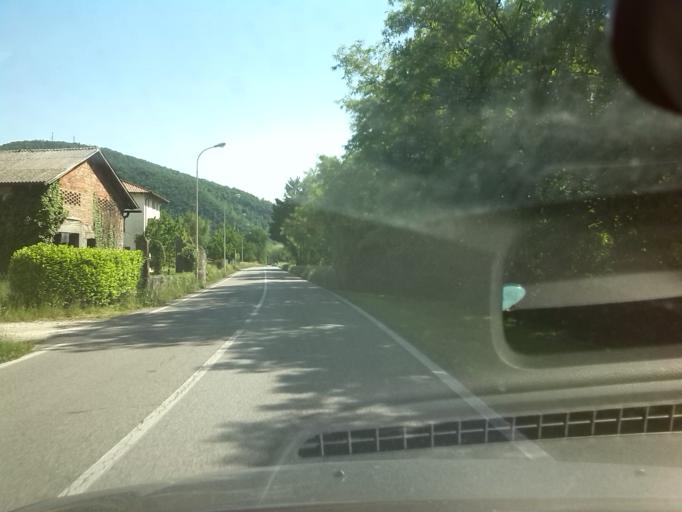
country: IT
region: Friuli Venezia Giulia
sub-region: Provincia di Udine
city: San Pietro al Natisone
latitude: 46.1219
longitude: 13.4821
